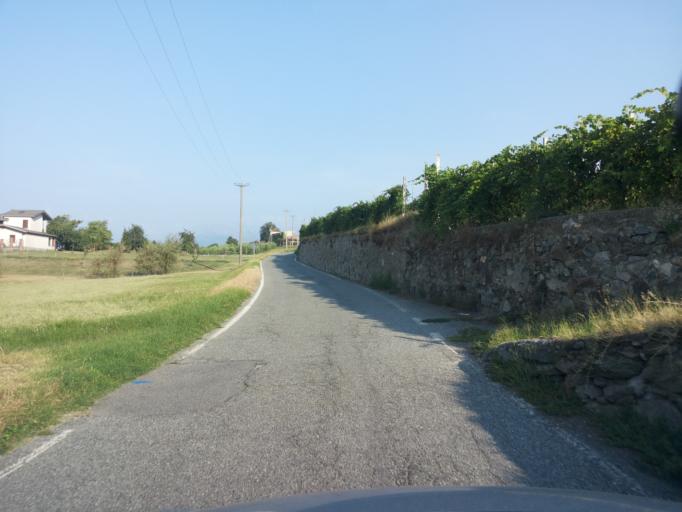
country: IT
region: Piedmont
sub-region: Provincia di Torino
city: Piverone
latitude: 45.4419
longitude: 8.0173
